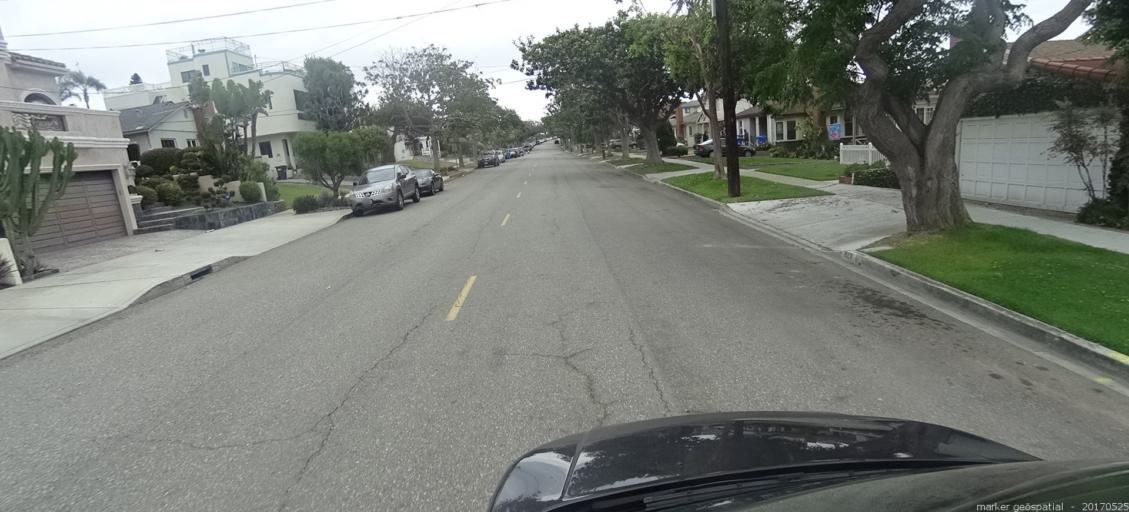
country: US
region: California
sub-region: Los Angeles County
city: Redondo Beach
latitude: 33.8543
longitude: -118.3874
